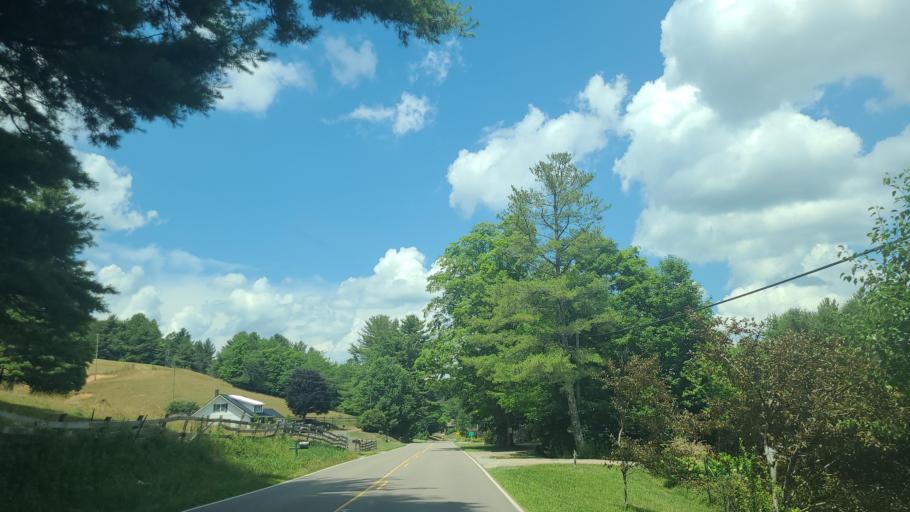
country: US
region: North Carolina
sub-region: Watauga County
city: Boone
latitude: 36.2372
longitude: -81.5452
